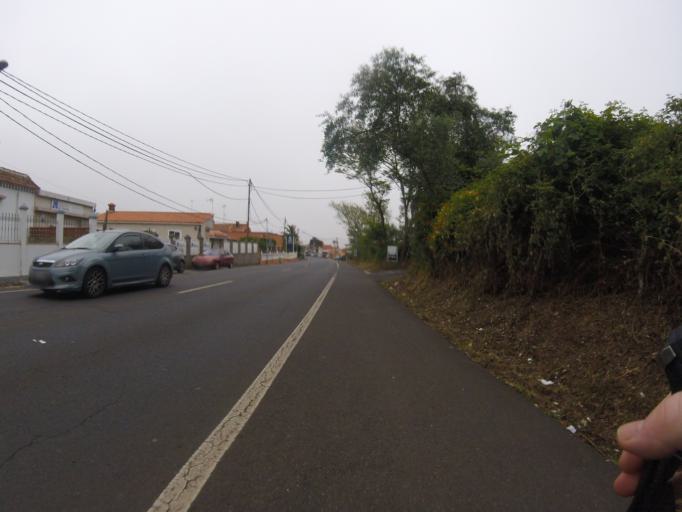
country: ES
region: Canary Islands
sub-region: Provincia de Santa Cruz de Tenerife
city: La Laguna
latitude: 28.4920
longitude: -16.3654
